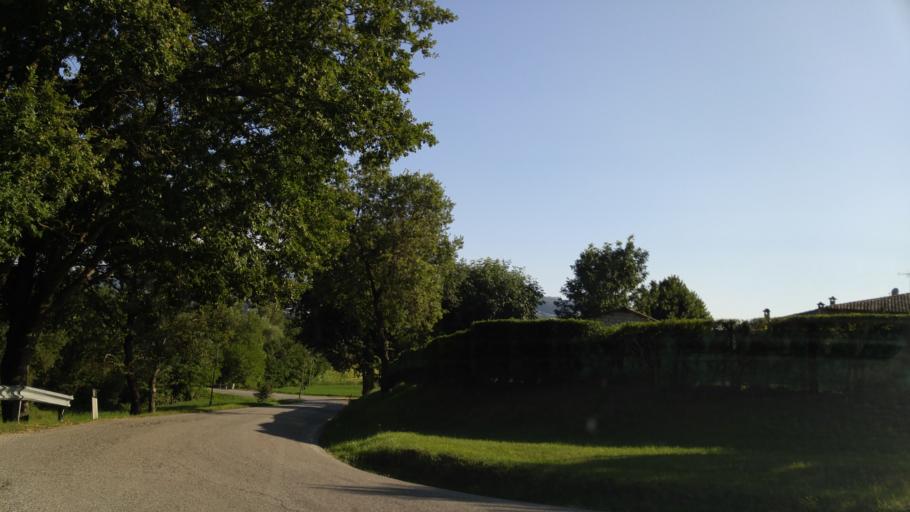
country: IT
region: The Marches
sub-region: Provincia di Pesaro e Urbino
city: Peglio
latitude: 43.6856
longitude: 12.5133
